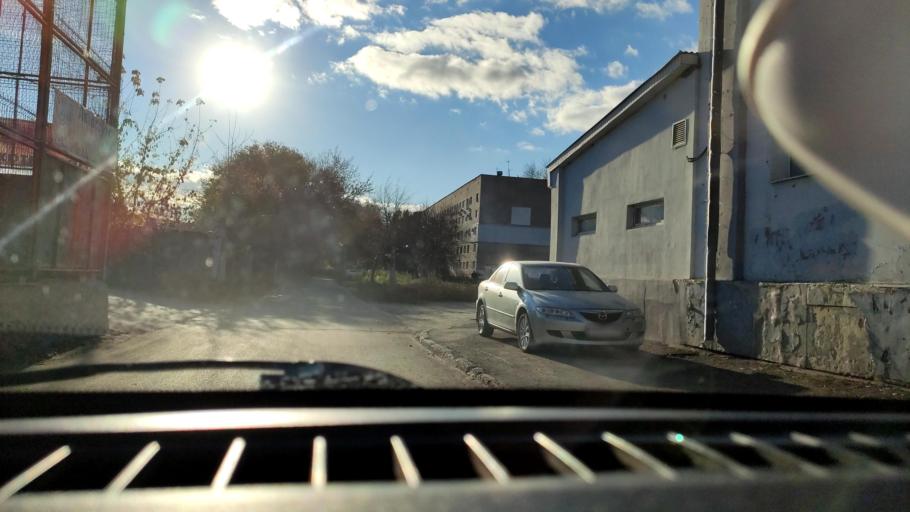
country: RU
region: Samara
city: Smyshlyayevka
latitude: 53.2166
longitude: 50.2758
